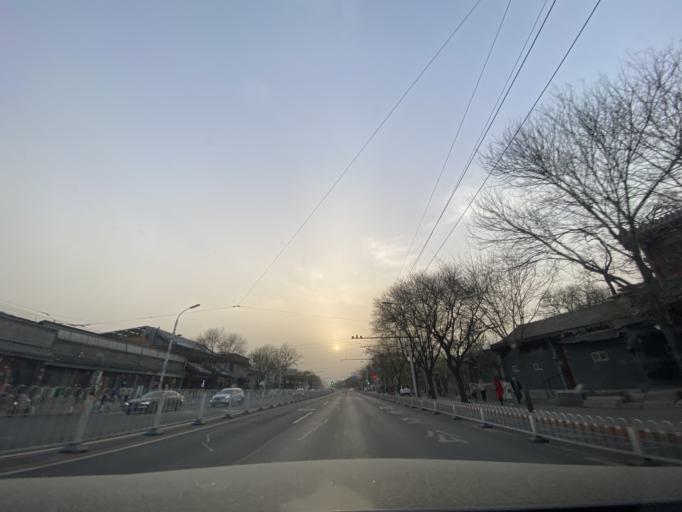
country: CN
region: Beijing
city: Jingshan
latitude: 39.9321
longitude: 116.3886
